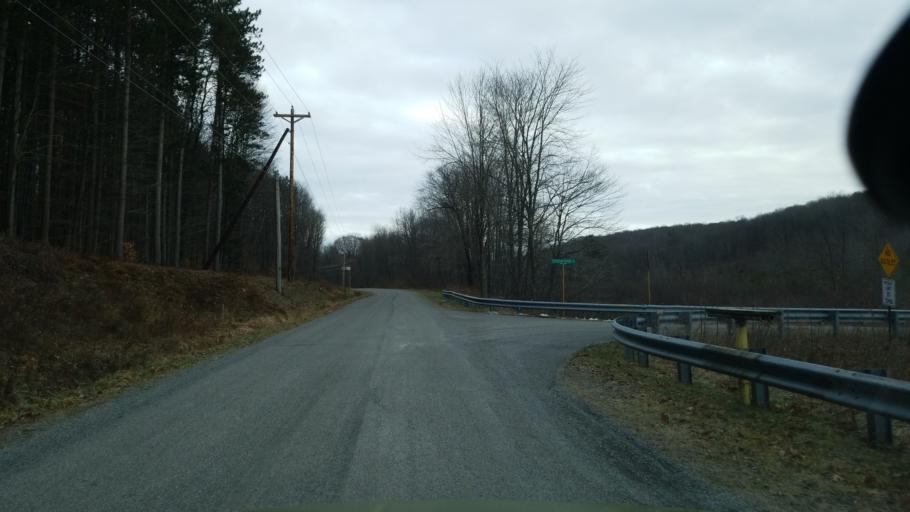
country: US
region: Pennsylvania
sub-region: Clearfield County
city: Treasure Lake
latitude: 41.1137
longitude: -78.6253
